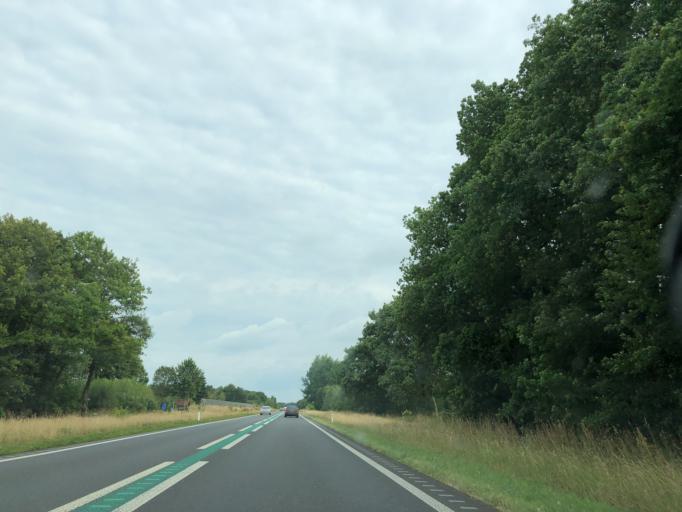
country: NL
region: Drenthe
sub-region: Gemeente Tynaarlo
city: Zuidlaren
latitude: 53.0773
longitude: 6.6771
